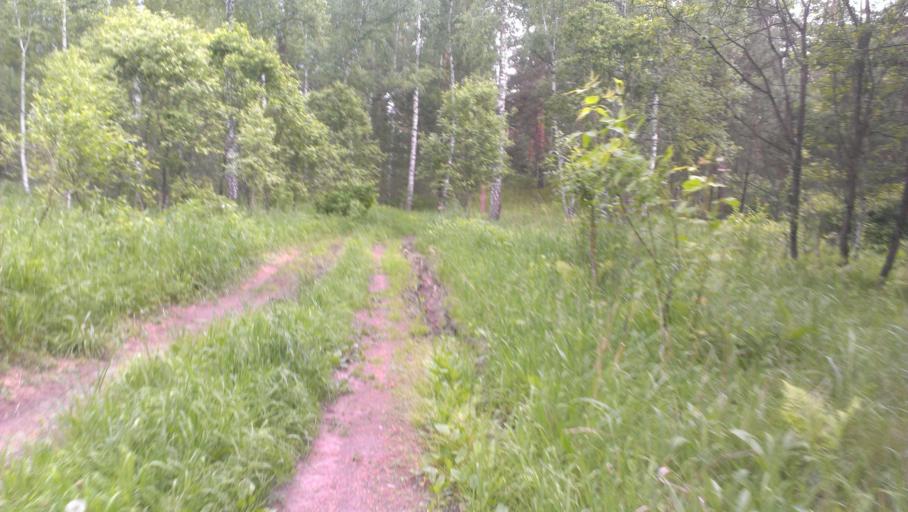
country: RU
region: Altai Krai
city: Sannikovo
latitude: 53.3483
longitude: 84.0390
